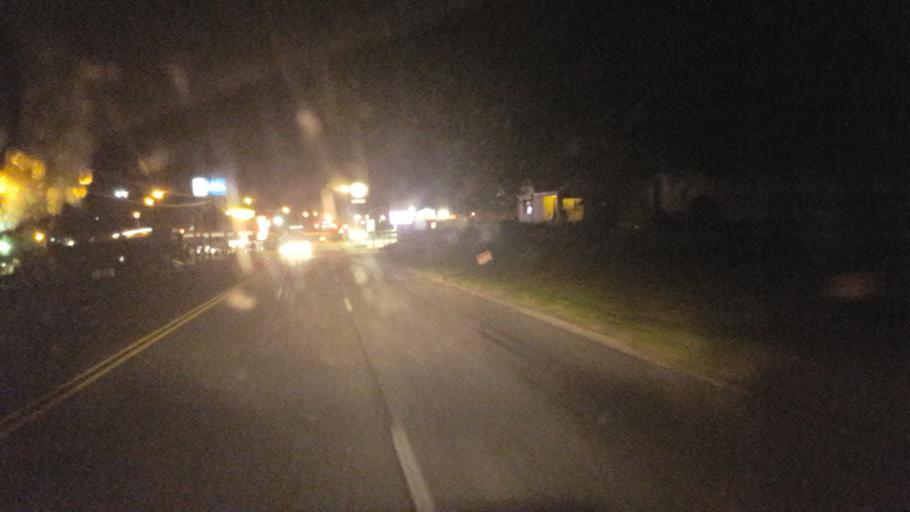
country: US
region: Ohio
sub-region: Tuscarawas County
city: New Philadelphia
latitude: 40.4933
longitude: -81.4708
